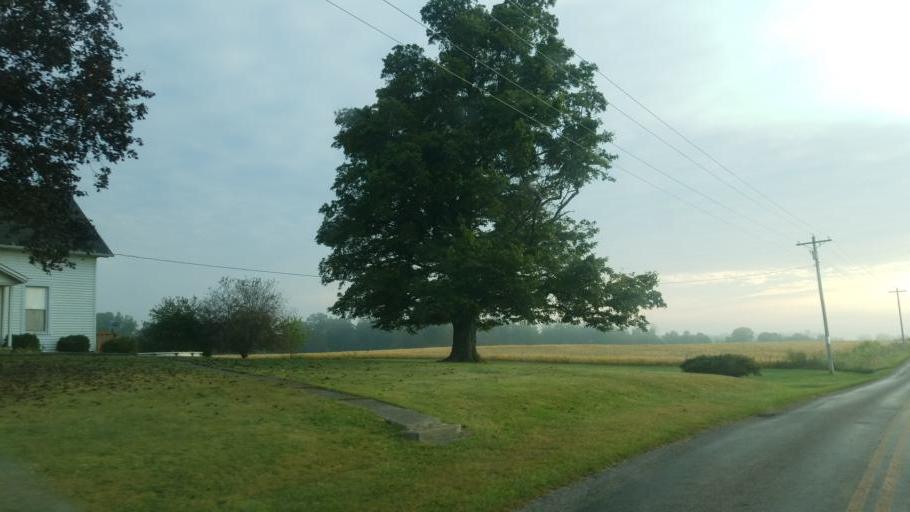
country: US
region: Ohio
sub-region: Knox County
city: Fredericktown
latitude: 40.4412
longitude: -82.6195
